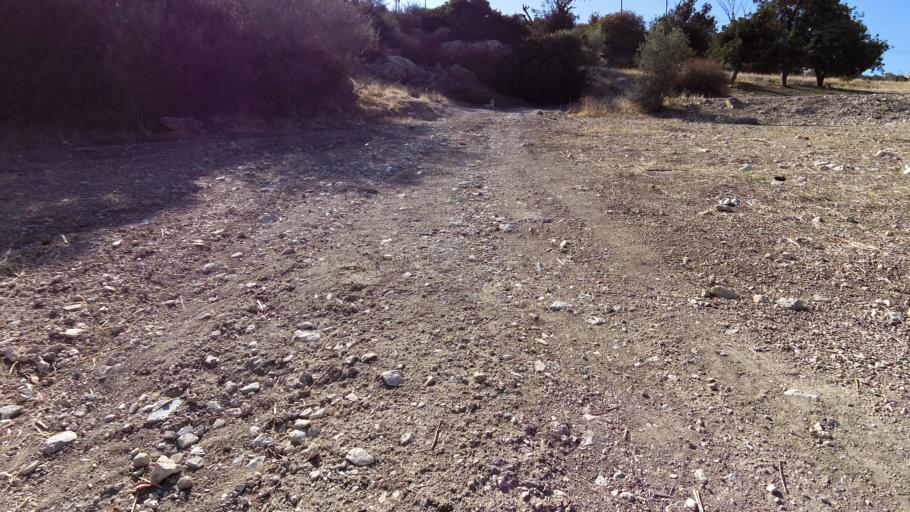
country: CY
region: Limassol
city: Mouttagiaka
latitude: 34.7595
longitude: 33.0884
